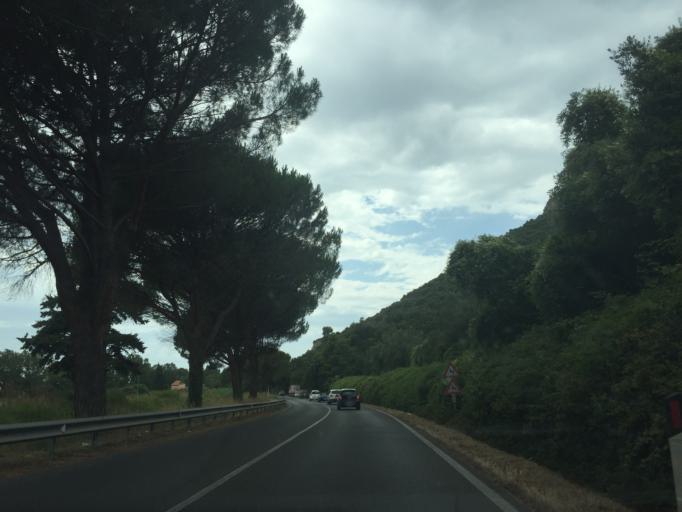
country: IT
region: Tuscany
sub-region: Province of Pisa
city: Asciano
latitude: 43.7523
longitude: 10.4512
